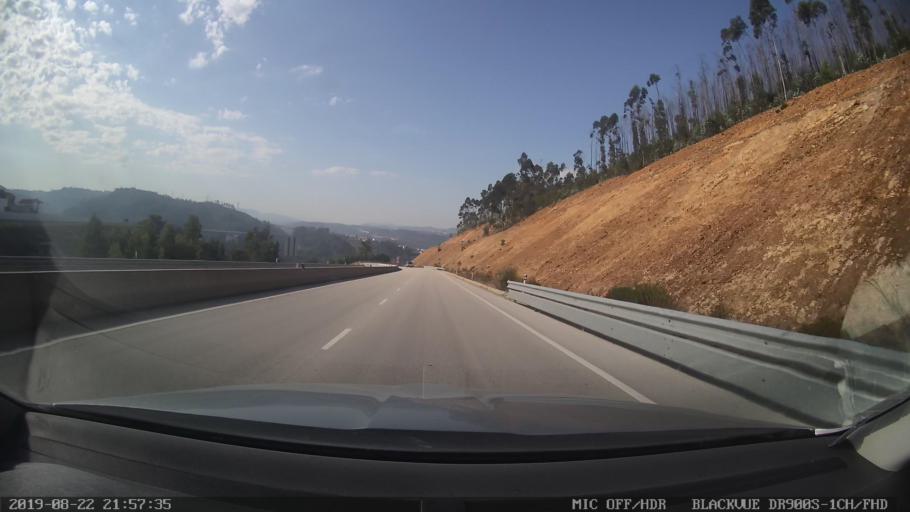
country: PT
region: Coimbra
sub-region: Coimbra
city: Coimbra
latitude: 40.1813
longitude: -8.3810
